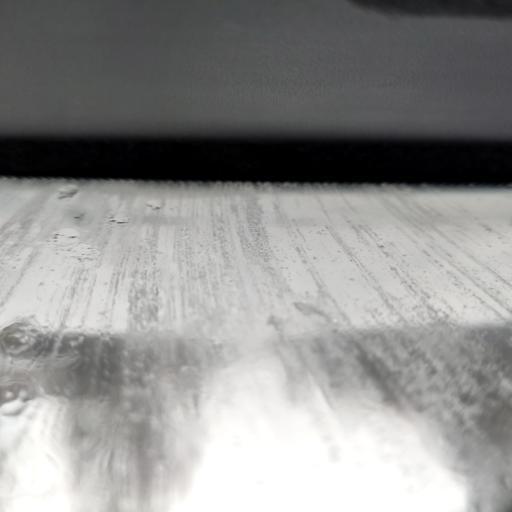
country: RU
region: Perm
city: Polazna
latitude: 58.1436
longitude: 56.4326
